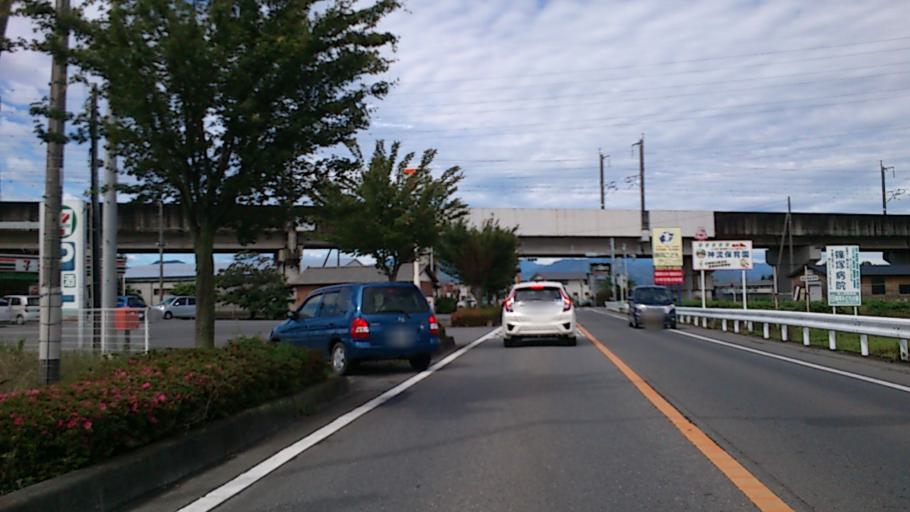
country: JP
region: Gunma
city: Fujioka
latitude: 36.2635
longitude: 139.0959
